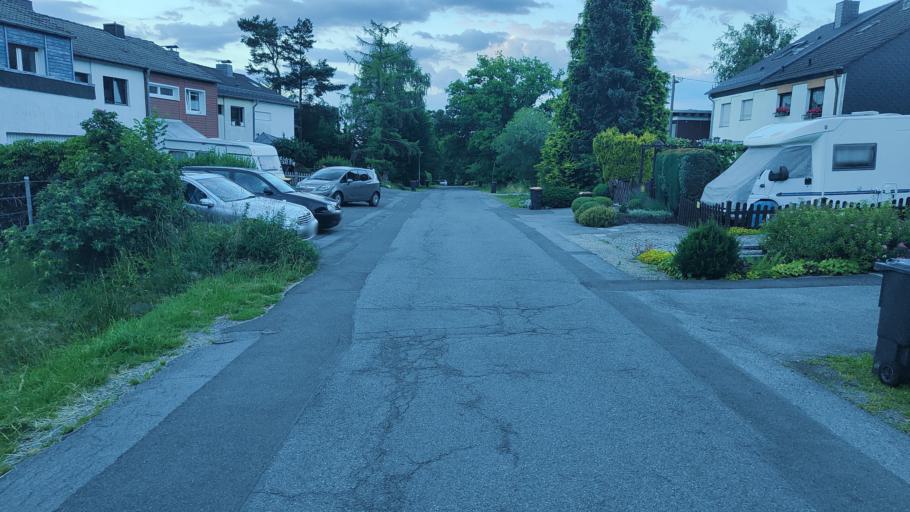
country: DE
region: North Rhine-Westphalia
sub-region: Regierungsbezirk Koln
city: Roetgen
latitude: 50.6327
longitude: 6.1839
